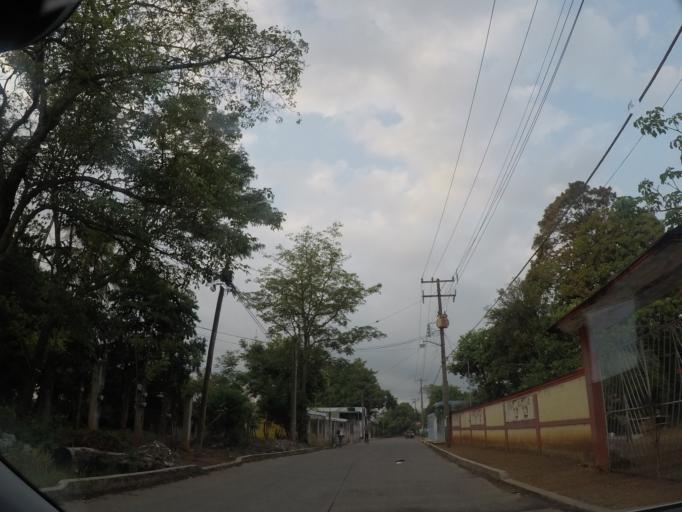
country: MX
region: Oaxaca
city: Matias Romero
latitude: 16.8713
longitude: -95.0353
